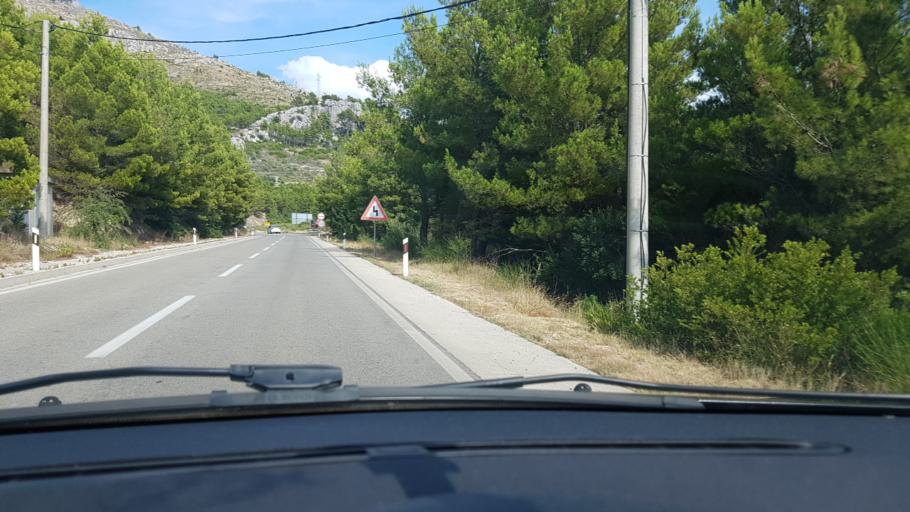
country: HR
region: Splitsko-Dalmatinska
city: Tucepi
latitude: 43.2826
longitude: 17.0396
